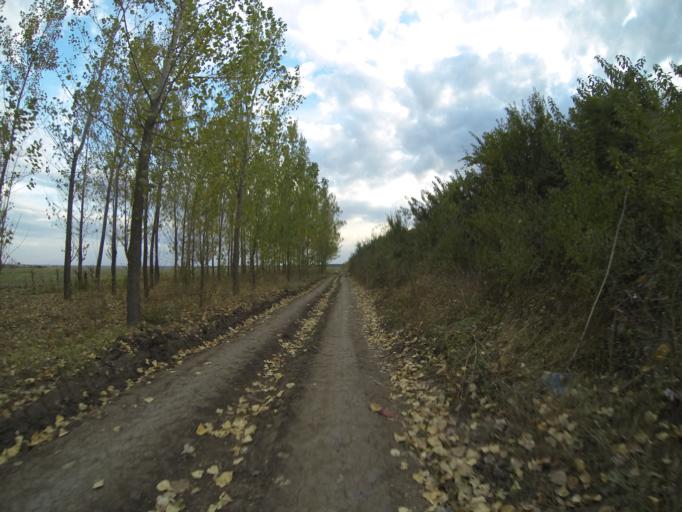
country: RO
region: Dolj
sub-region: Comuna Ceratu
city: Ceratu
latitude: 44.1057
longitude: 23.6934
